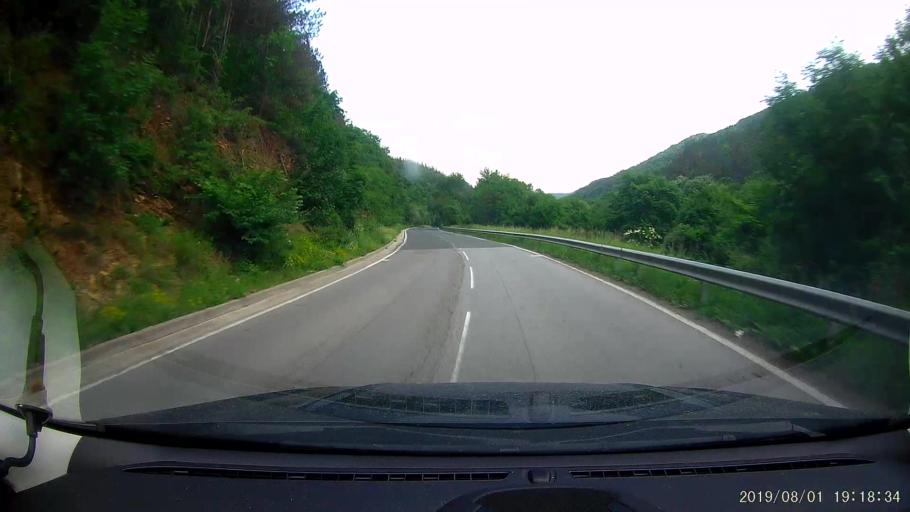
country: BG
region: Shumen
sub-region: Obshtina Smyadovo
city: Smyadovo
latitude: 42.9115
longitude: 26.9397
